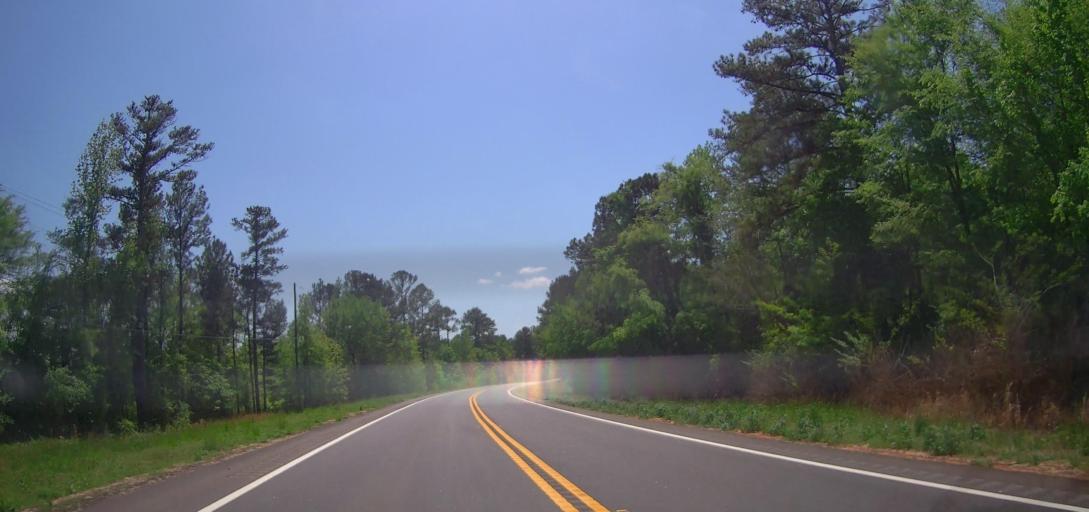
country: US
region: Georgia
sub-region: Putnam County
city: Eatonton
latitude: 33.2645
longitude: -83.4146
